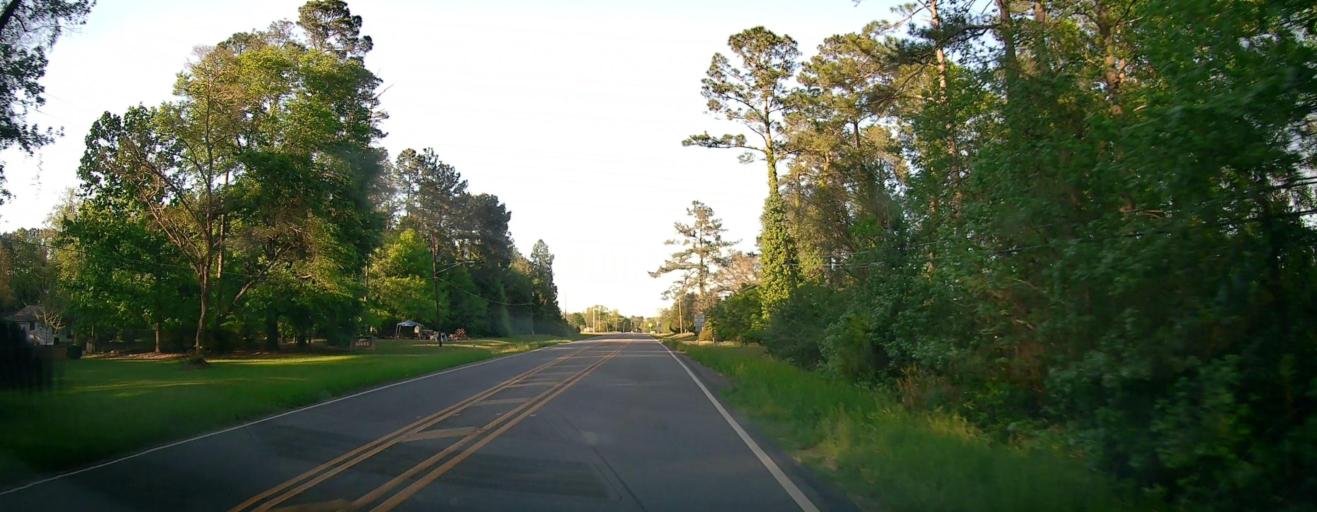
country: US
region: Georgia
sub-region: Macon County
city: Oglethorpe
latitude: 32.2854
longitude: -84.0700
